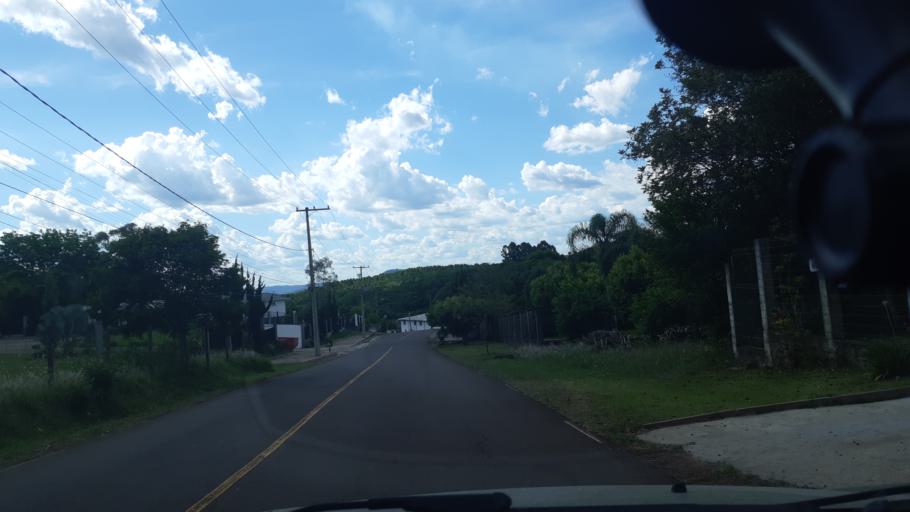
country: BR
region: Rio Grande do Sul
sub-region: Novo Hamburgo
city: Novo Hamburgo
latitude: -29.6228
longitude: -51.1096
